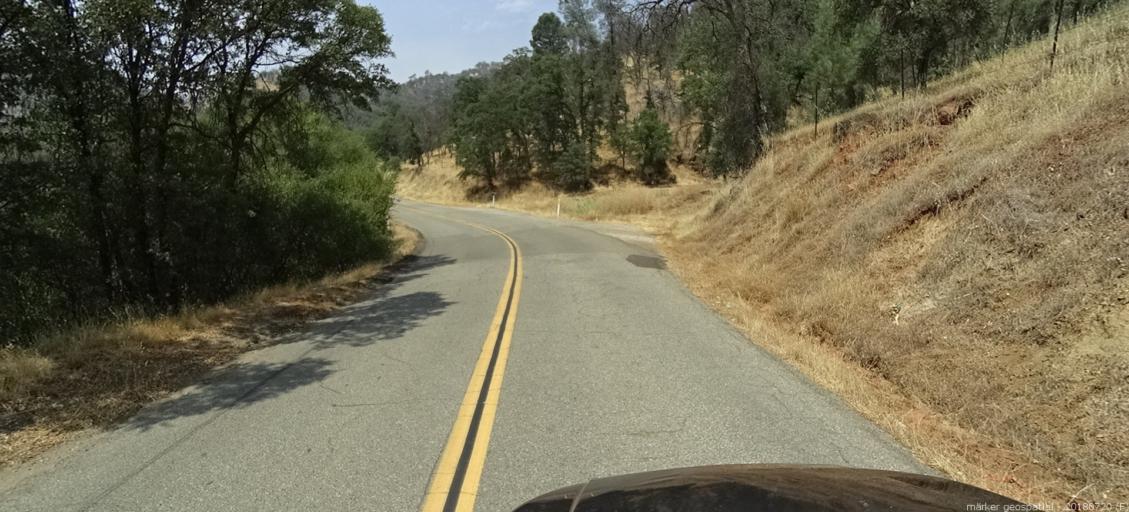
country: US
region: California
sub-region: Madera County
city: Ahwahnee
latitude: 37.3482
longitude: -119.7563
